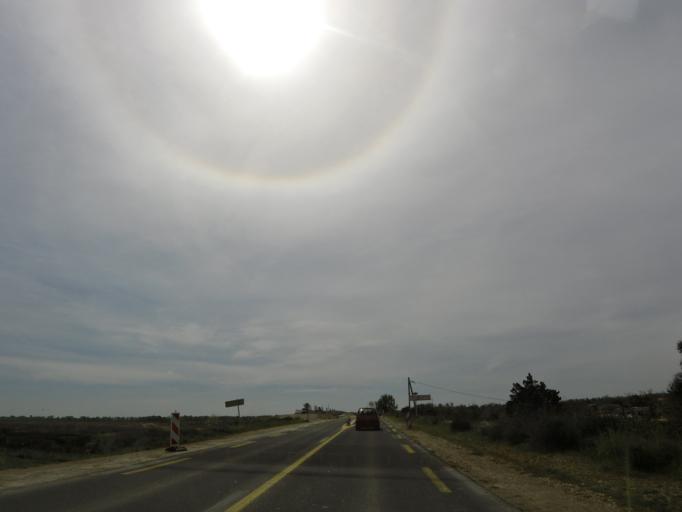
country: FR
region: Languedoc-Roussillon
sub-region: Departement de l'Herault
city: La Grande-Motte
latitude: 43.5873
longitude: 4.1044
